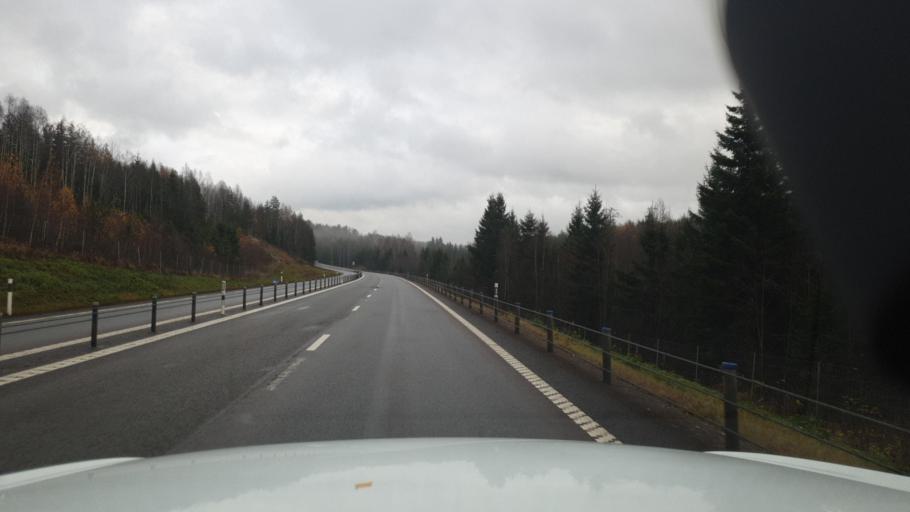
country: SE
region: Vaermland
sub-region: Arvika Kommun
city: Arvika
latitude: 59.6432
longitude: 12.7337
